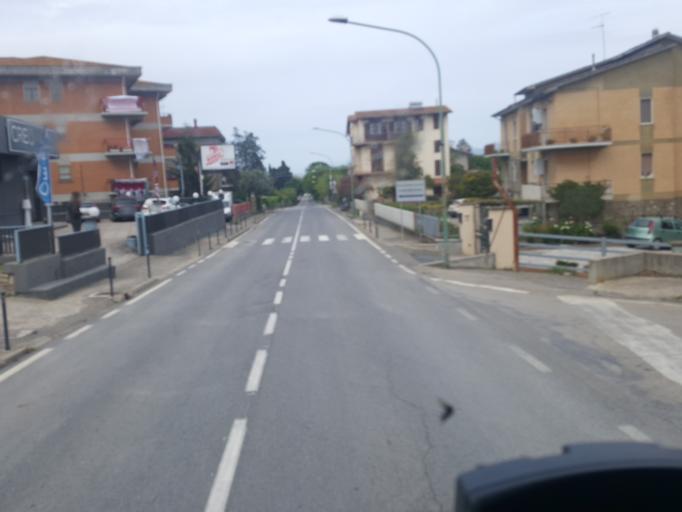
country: IT
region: Latium
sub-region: Provincia di Viterbo
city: Monte Romano
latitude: 42.2710
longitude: 11.9039
